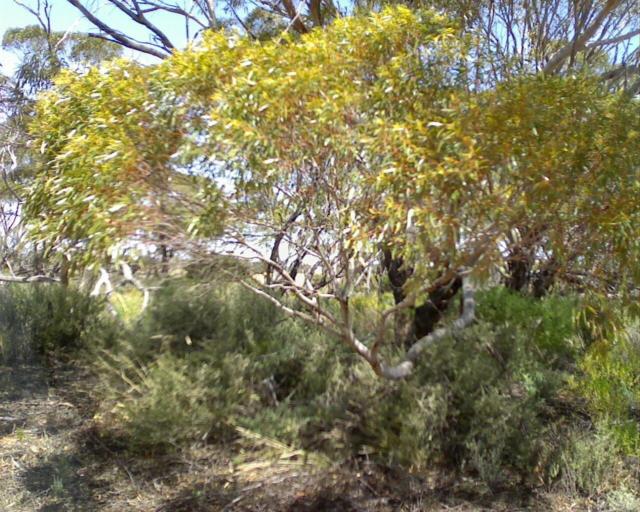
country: AU
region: South Australia
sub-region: Kimba
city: Caralue
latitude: -32.9467
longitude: 135.2830
